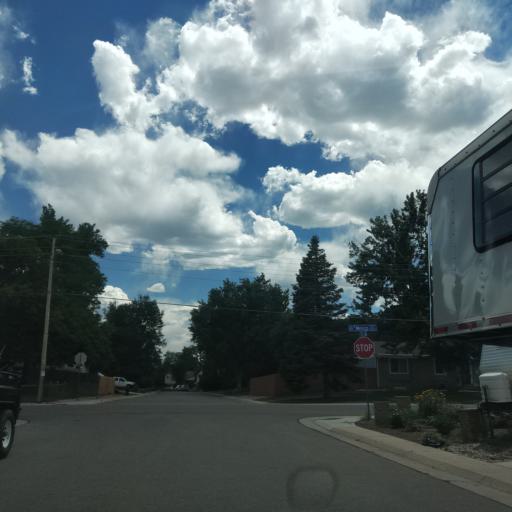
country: US
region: Colorado
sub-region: Jefferson County
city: Lakewood
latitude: 39.6860
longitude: -105.0984
